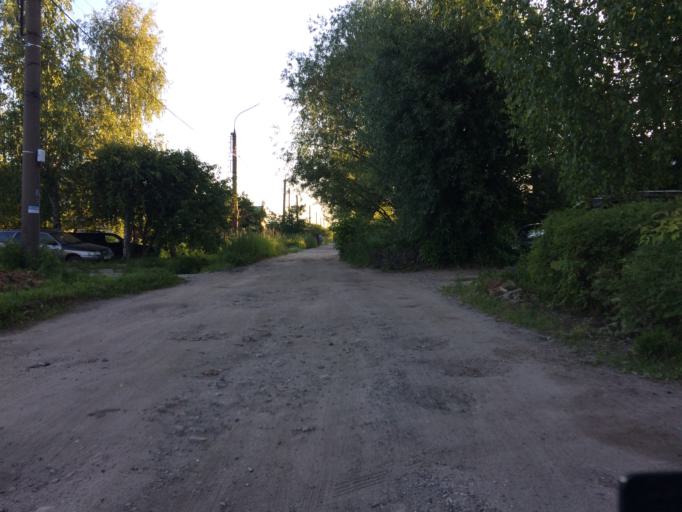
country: RU
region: Mariy-El
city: Yoshkar-Ola
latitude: 56.6530
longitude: 47.8968
